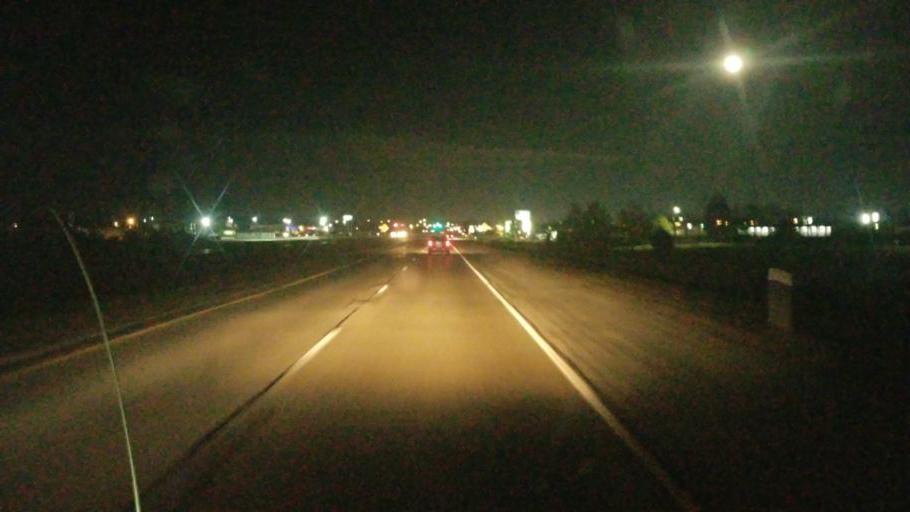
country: US
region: Indiana
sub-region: Decatur County
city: Greensburg
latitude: 39.3455
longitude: -85.5017
